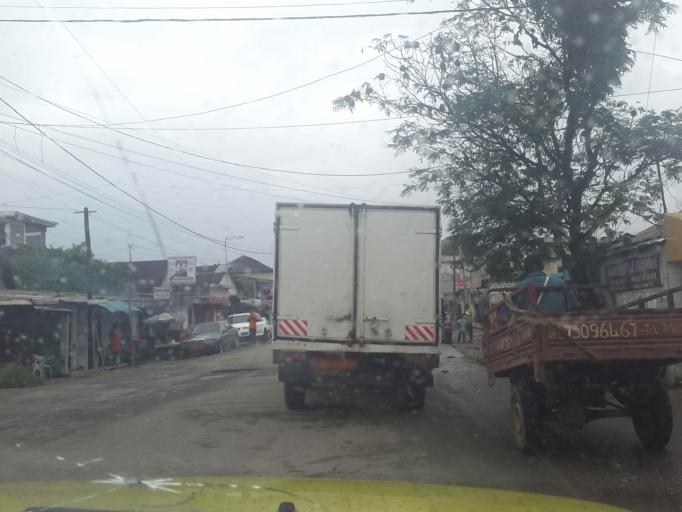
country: CM
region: Littoral
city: Douala
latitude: 4.0689
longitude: 9.7120
